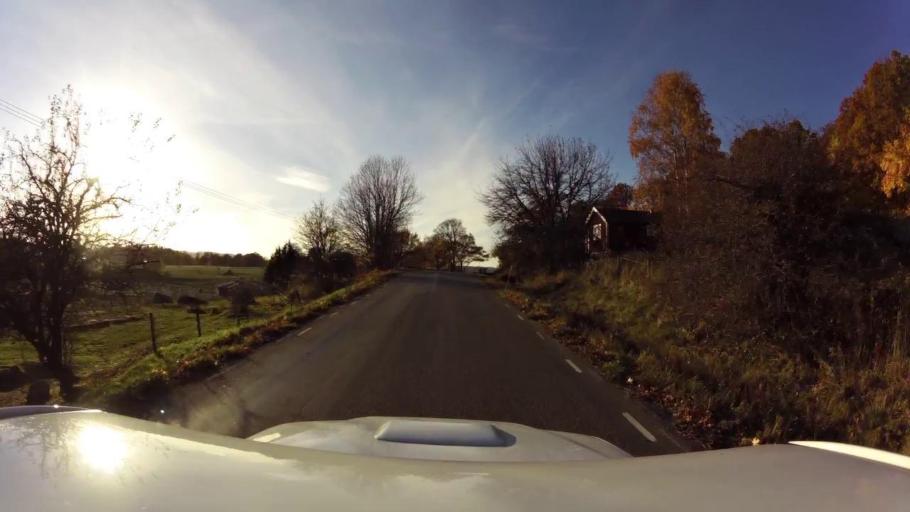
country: SE
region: OEstergoetland
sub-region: Kinda Kommun
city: Rimforsa
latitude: 58.1736
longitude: 15.6800
